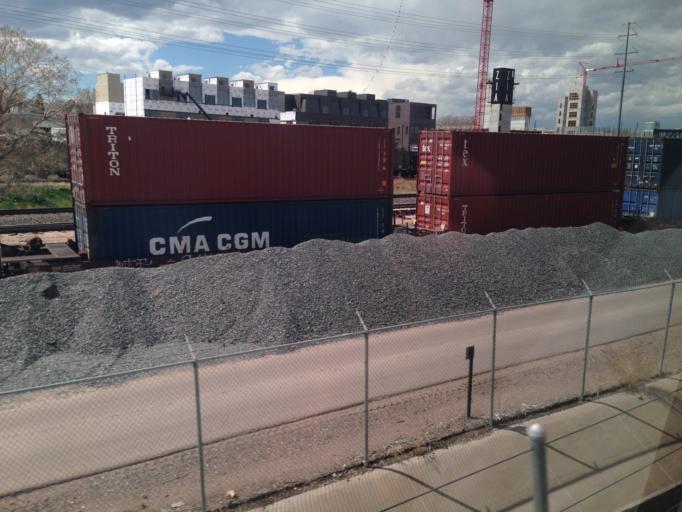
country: US
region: Colorado
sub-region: Denver County
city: Denver
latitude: 39.7707
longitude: -104.9971
